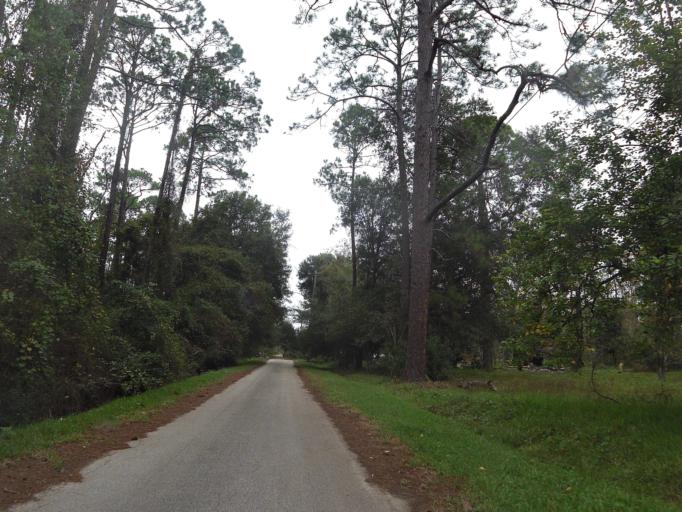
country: US
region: Florida
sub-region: Duval County
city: Baldwin
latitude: 30.2590
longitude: -81.8739
